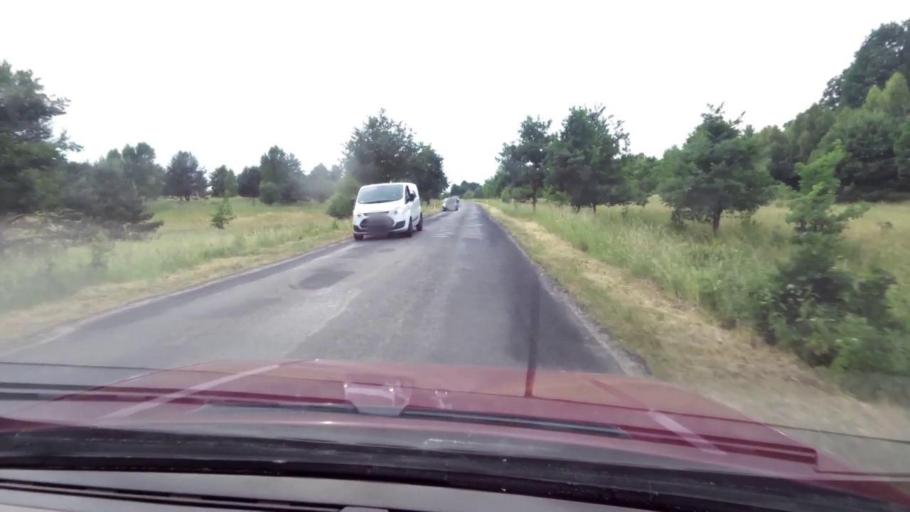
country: PL
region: Pomeranian Voivodeship
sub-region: Powiat slupski
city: Kepice
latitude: 54.2745
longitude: 16.9775
